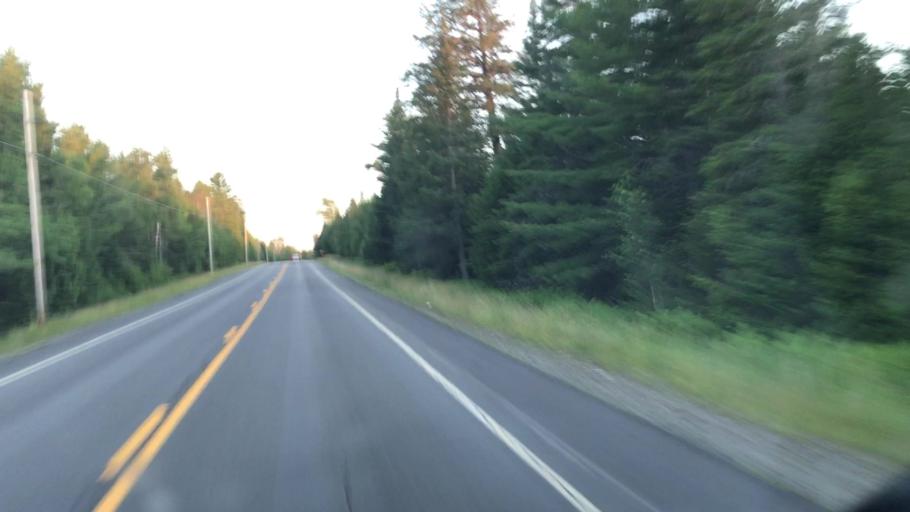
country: US
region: Maine
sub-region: Penobscot County
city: Medway
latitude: 45.5714
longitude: -68.3211
